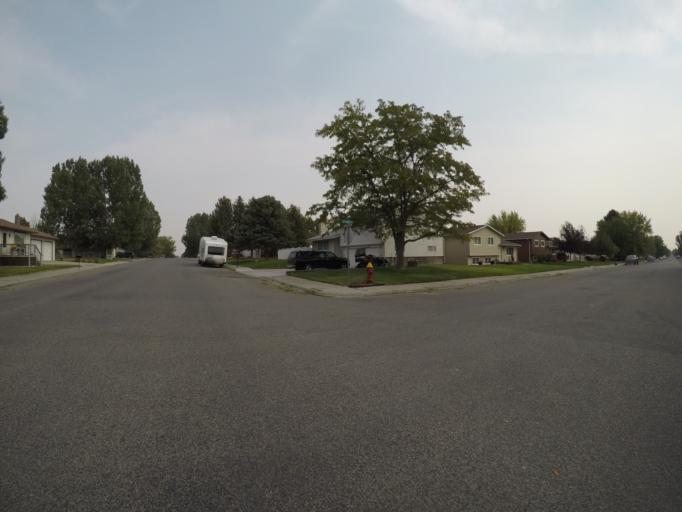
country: US
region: Montana
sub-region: Yellowstone County
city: Laurel
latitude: 45.6792
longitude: -108.7805
